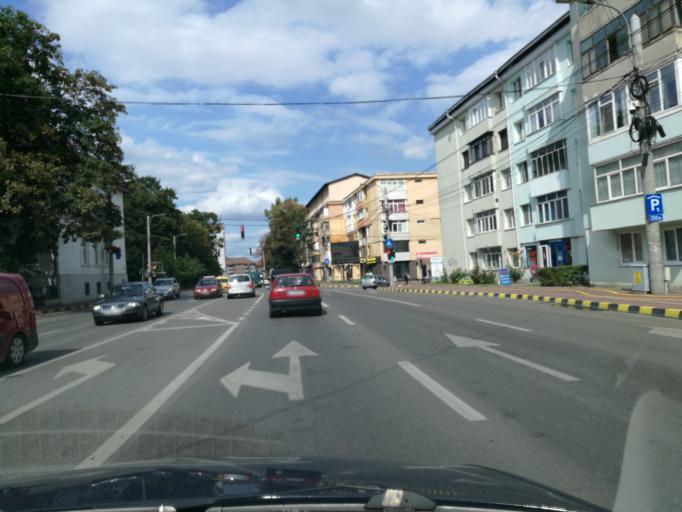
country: RO
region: Suceava
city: Suceava
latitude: 47.6414
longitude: 26.2598
